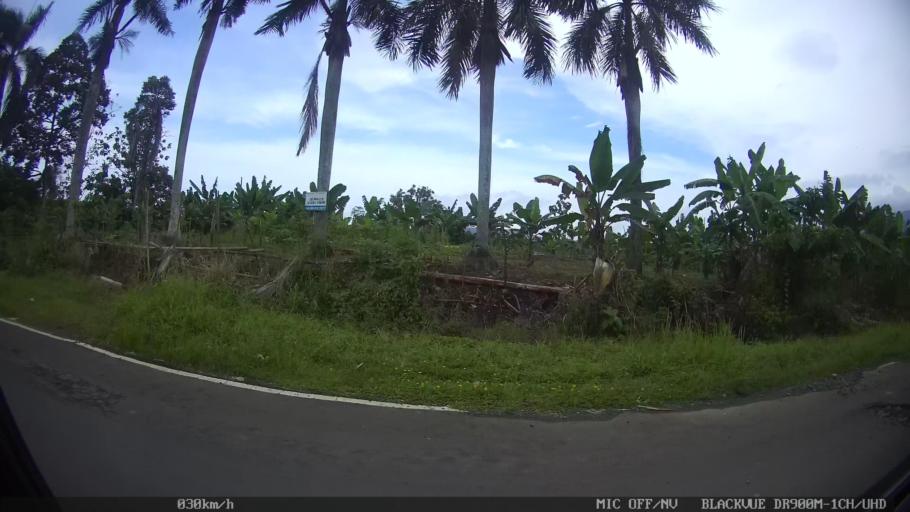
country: ID
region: Lampung
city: Bandarlampung
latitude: -5.4360
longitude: 105.2156
